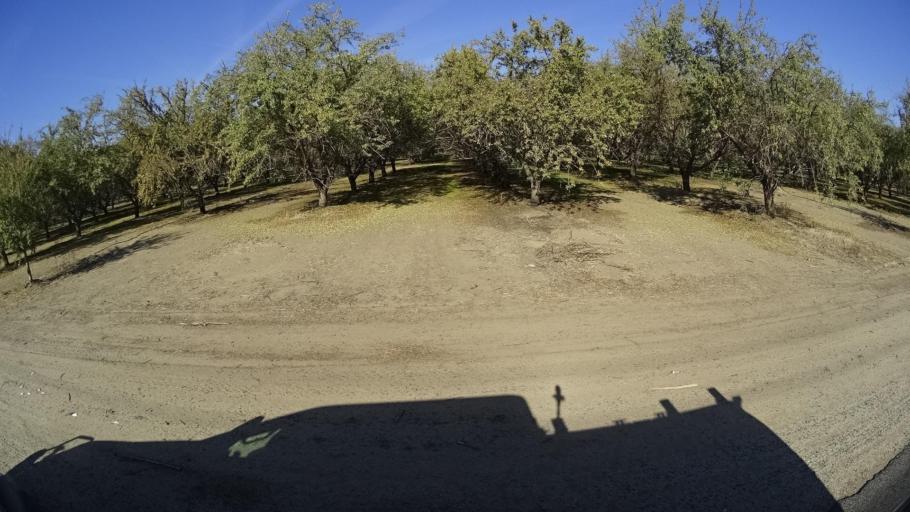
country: US
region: California
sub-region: Kern County
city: McFarland
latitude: 35.6454
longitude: -119.2487
